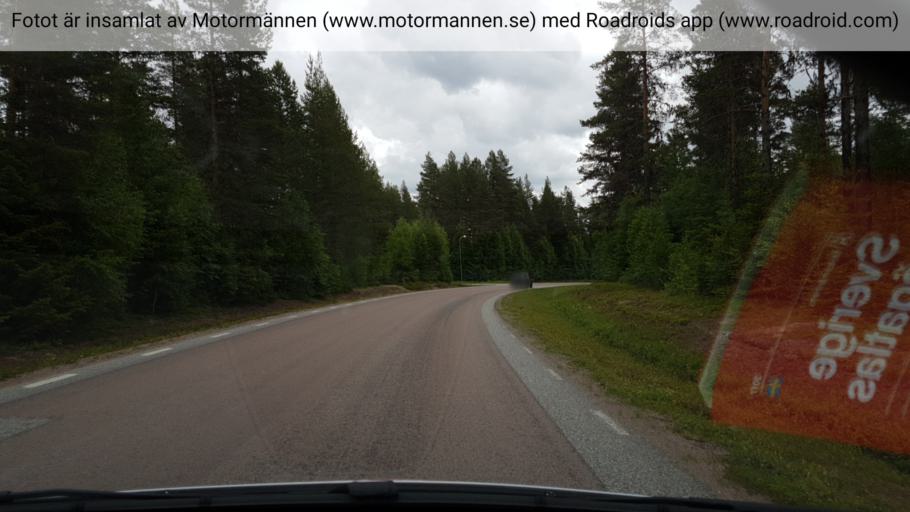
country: SE
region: Vaesternorrland
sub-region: Solleftea Kommun
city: As
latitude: 63.6815
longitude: 16.9916
